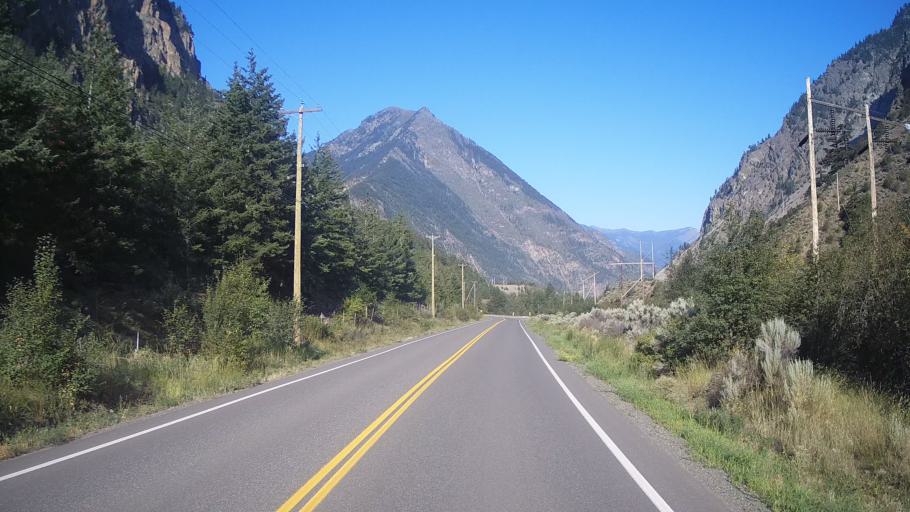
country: CA
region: British Columbia
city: Lillooet
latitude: 50.6692
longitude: -121.9549
